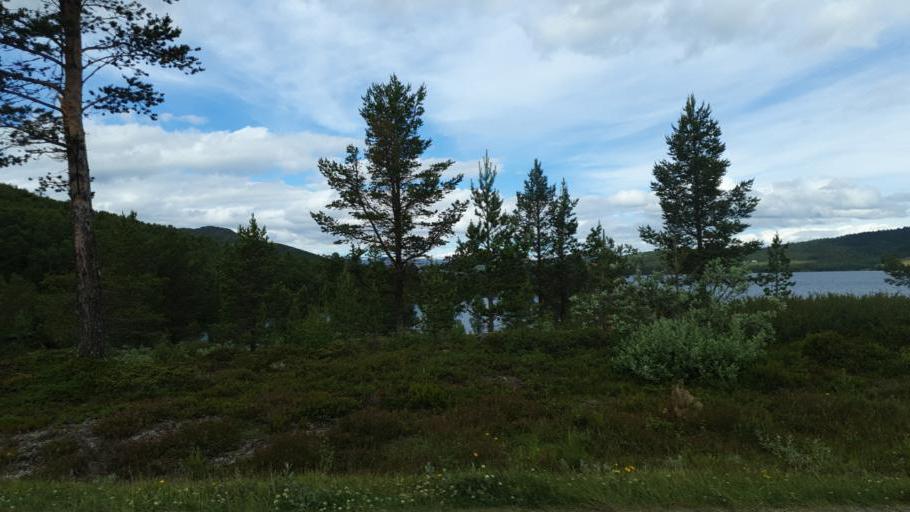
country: NO
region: Oppland
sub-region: Vaga
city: Vagamo
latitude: 61.7592
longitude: 9.0733
